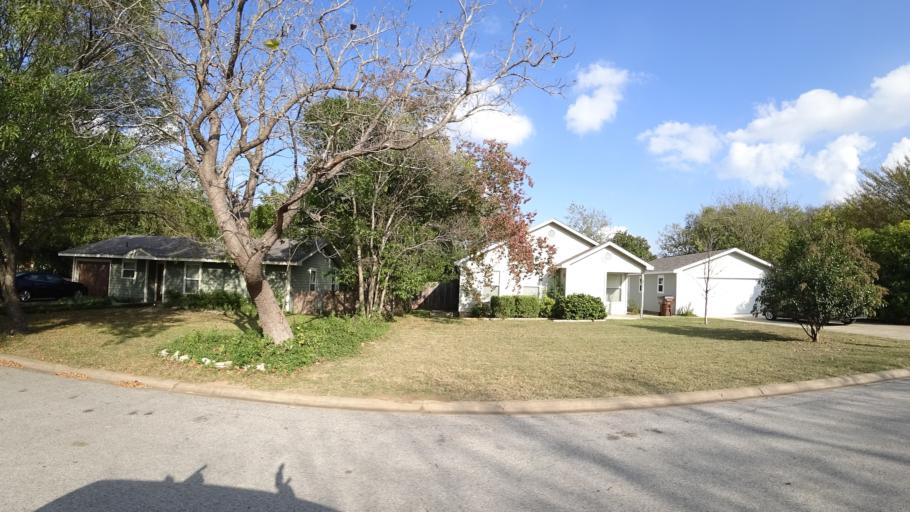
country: US
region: Texas
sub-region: Williamson County
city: Round Rock
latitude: 30.4901
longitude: -97.6720
